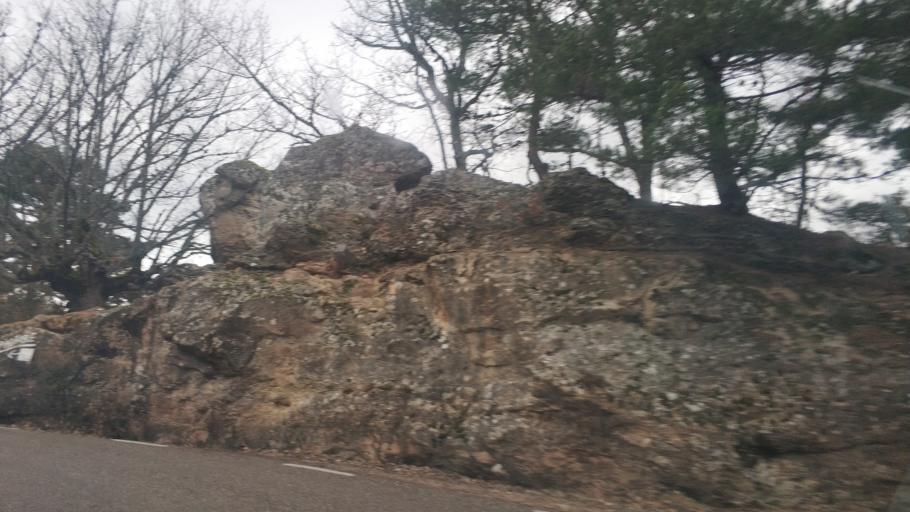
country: ES
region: Castille and Leon
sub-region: Provincia de Burgos
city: Canicosa de la Sierra
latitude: 41.9316
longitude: -3.0390
